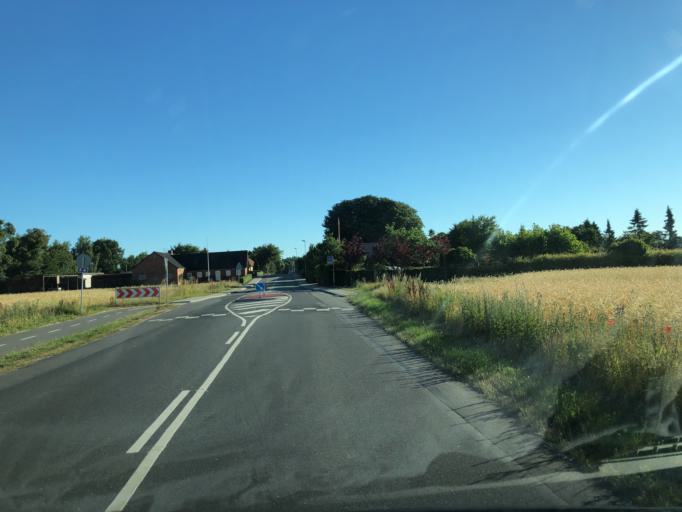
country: DK
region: Central Jutland
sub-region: Viborg Kommune
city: Stoholm
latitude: 56.4715
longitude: 9.2267
